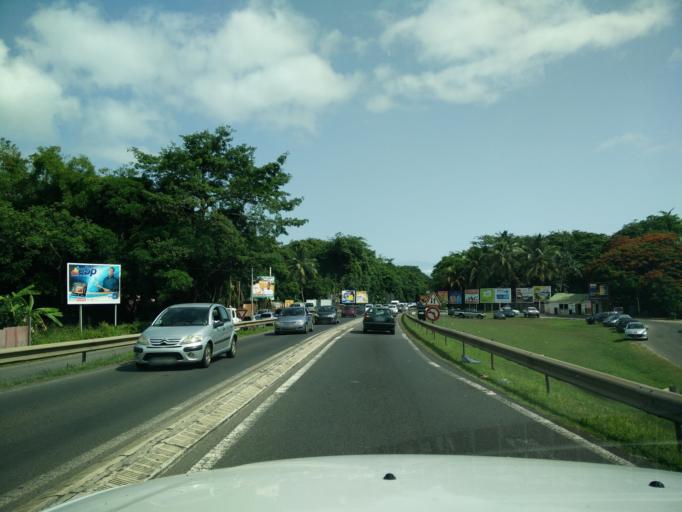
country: GP
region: Guadeloupe
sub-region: Guadeloupe
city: Baie-Mahault
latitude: 16.2525
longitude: -61.5707
